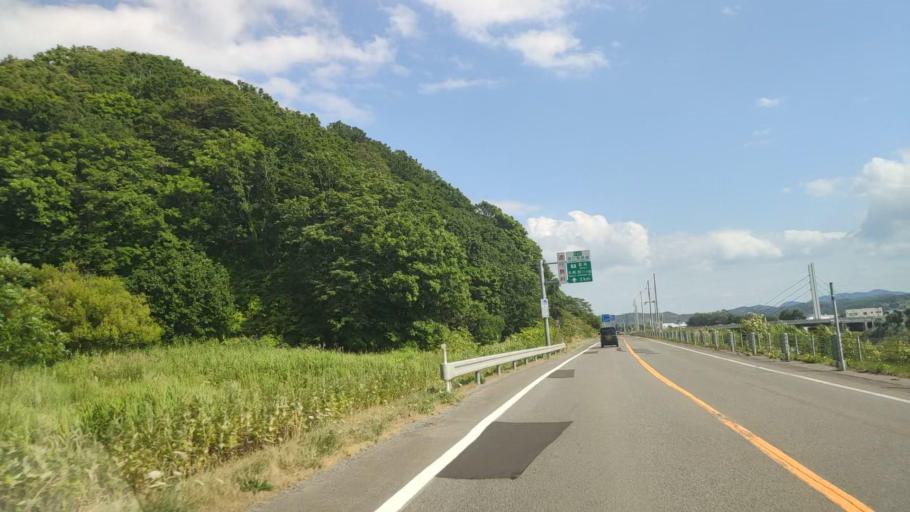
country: JP
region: Hokkaido
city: Rumoi
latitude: 43.9500
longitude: 141.6479
